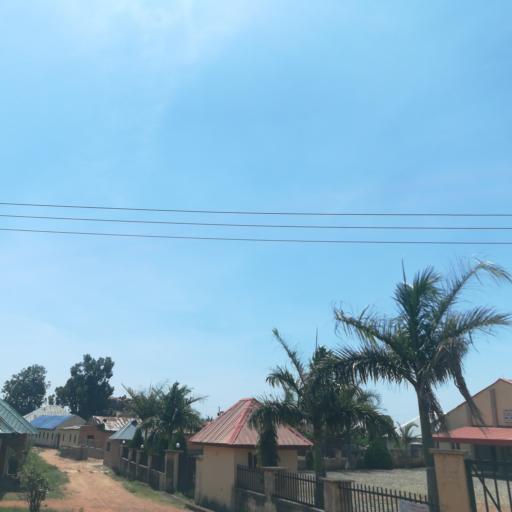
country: NG
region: Plateau
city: Bukuru
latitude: 9.7857
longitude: 8.8796
